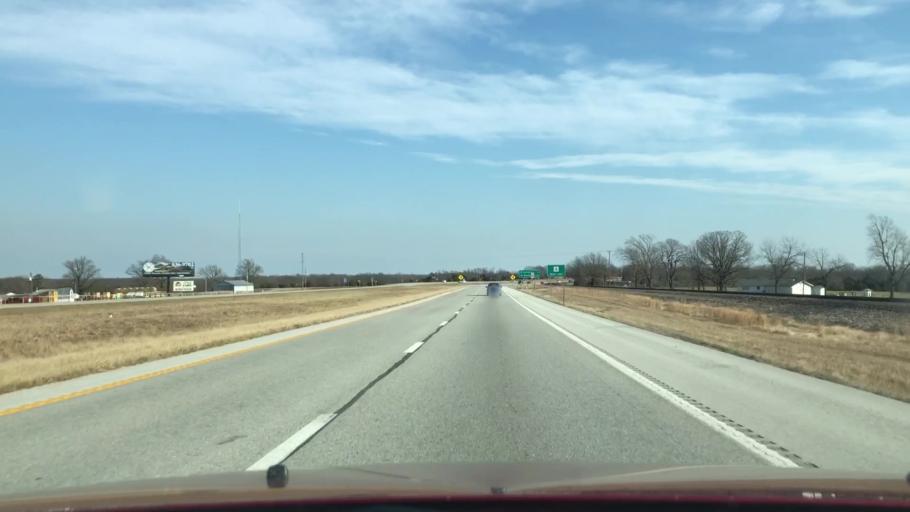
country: US
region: Missouri
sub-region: Webster County
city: Seymour
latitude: 37.1698
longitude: -92.8671
